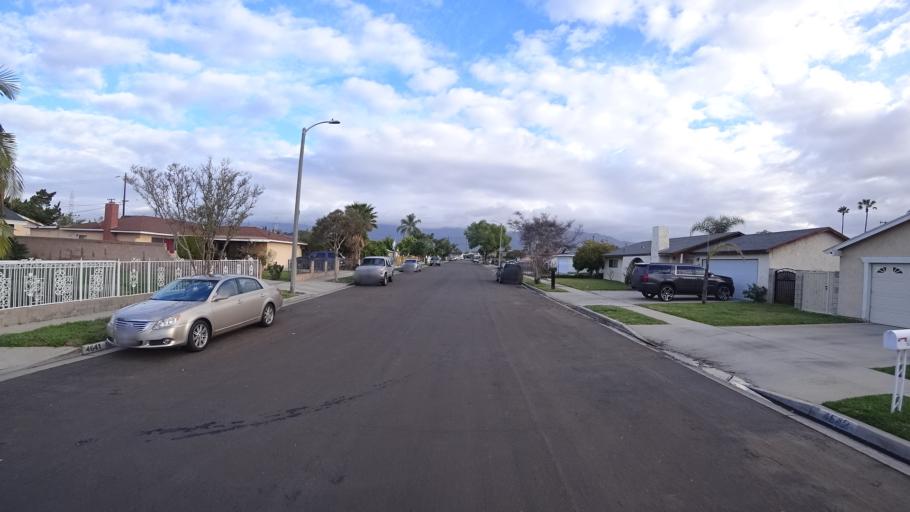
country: US
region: California
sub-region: Los Angeles County
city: Baldwin Park
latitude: 34.0967
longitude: -117.9747
